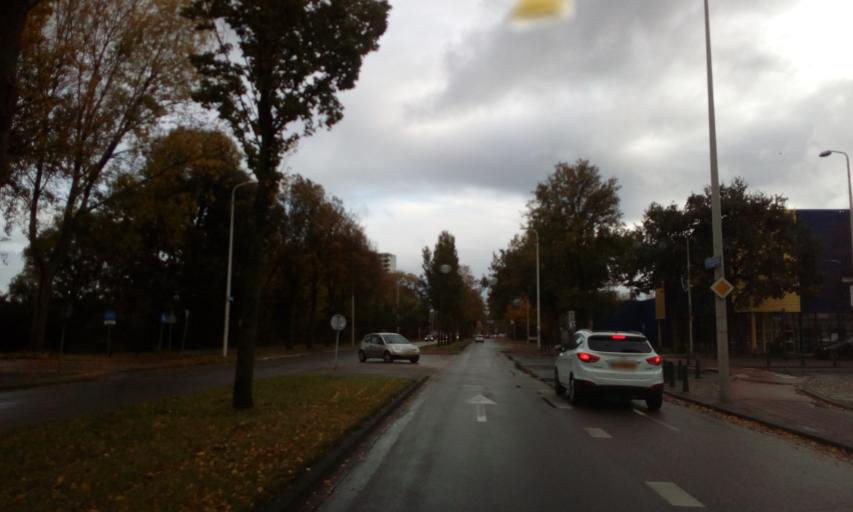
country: NL
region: South Holland
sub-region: Gemeente Westland
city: Kwintsheul
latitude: 52.0530
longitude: 4.2591
